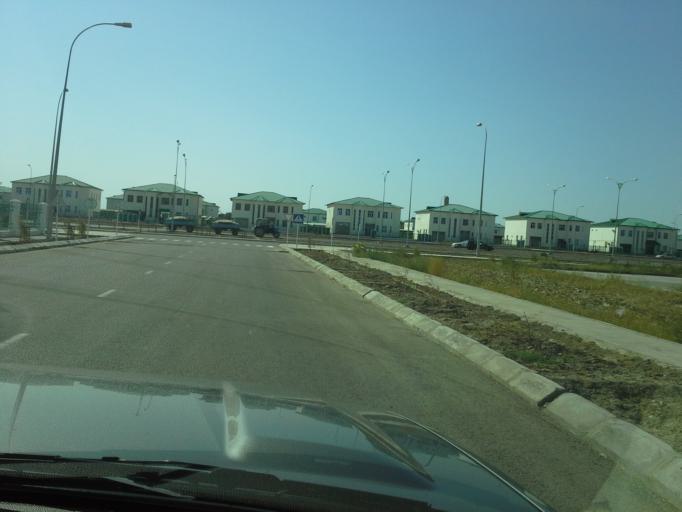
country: TM
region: Dasoguz
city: Dasoguz
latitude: 41.8143
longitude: 59.9531
